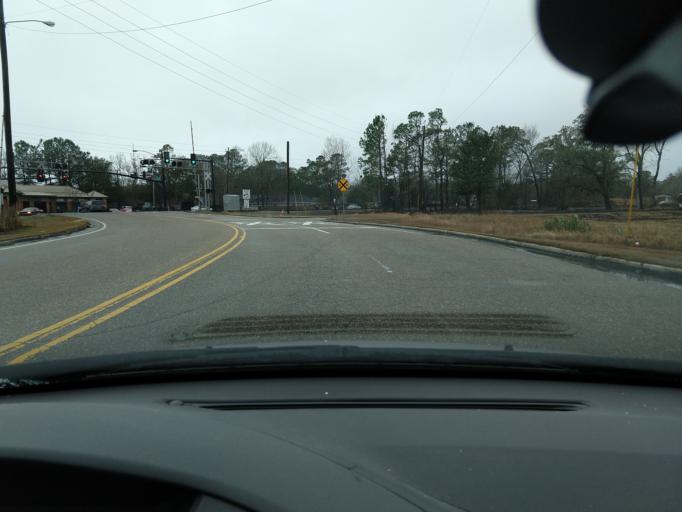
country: US
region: Mississippi
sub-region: Jackson County
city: Gulf Park Estates
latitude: 30.4111
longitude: -88.7855
